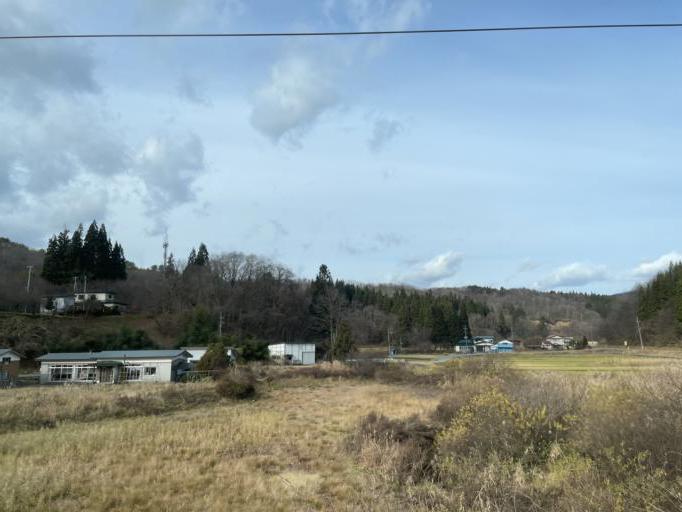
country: JP
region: Akita
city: Akita
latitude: 39.6661
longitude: 140.2783
